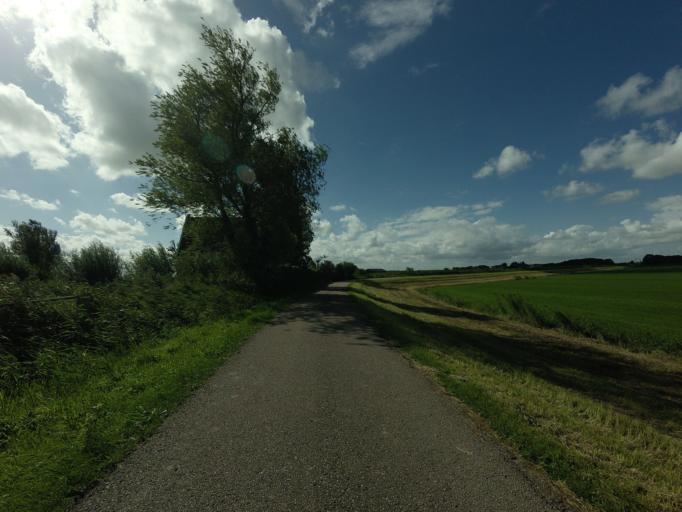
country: NL
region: North Holland
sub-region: Gemeente Hoorn
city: Hoorn
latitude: 52.5951
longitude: 5.0135
